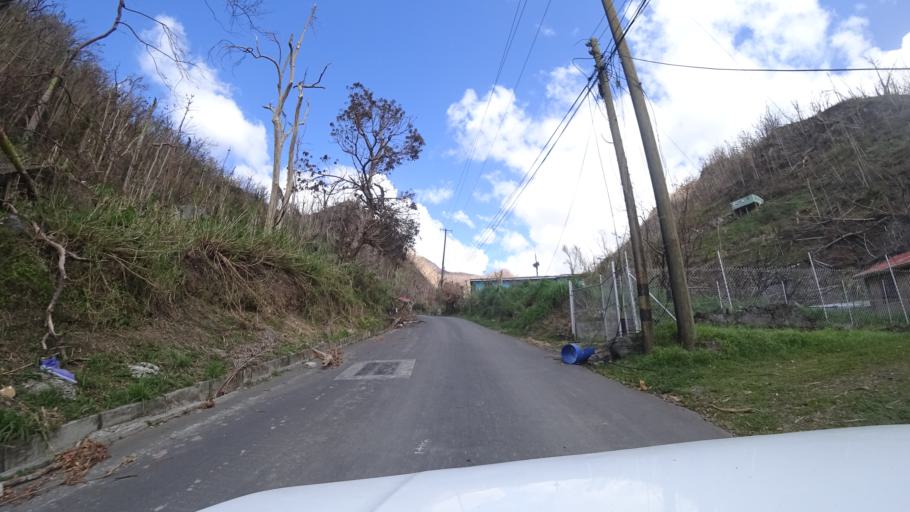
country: DM
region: Saint Luke
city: Pointe Michel
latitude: 15.2756
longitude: -61.3640
